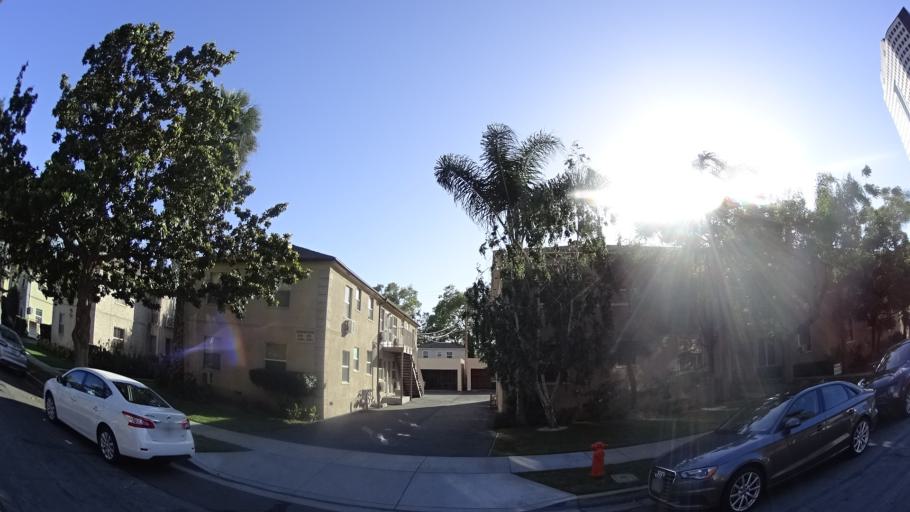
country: US
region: California
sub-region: Los Angeles County
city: Universal City
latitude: 34.1517
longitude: -118.3412
